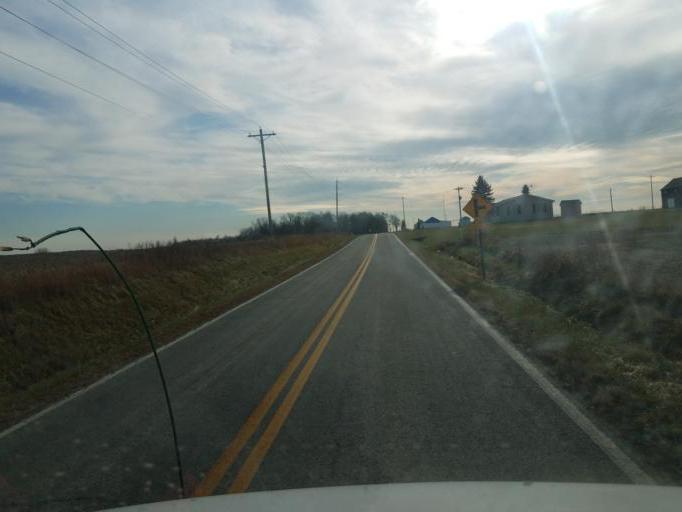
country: US
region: Ohio
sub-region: Delaware County
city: Ashley
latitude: 40.3487
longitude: -82.9662
